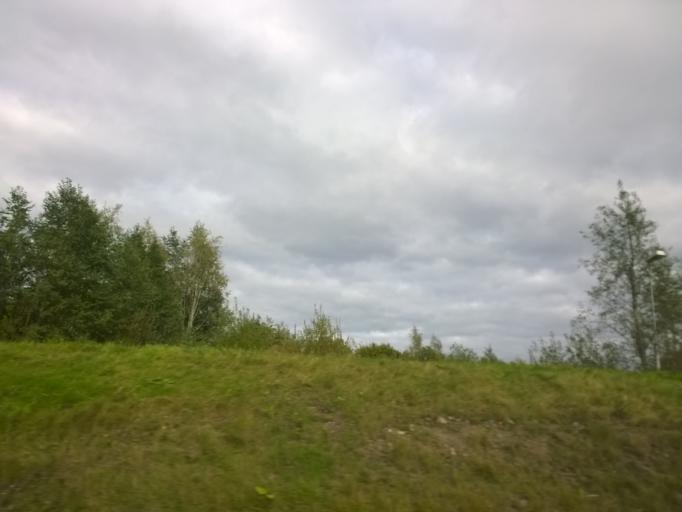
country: FI
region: Pirkanmaa
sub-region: Tampere
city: Tampere
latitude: 61.4827
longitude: 23.8287
